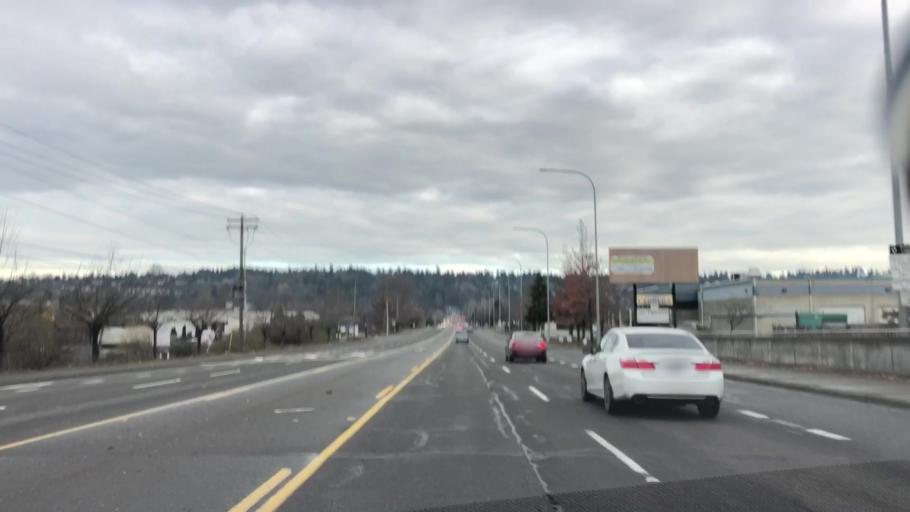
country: US
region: Washington
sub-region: King County
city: Kent
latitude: 47.4120
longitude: -122.2356
